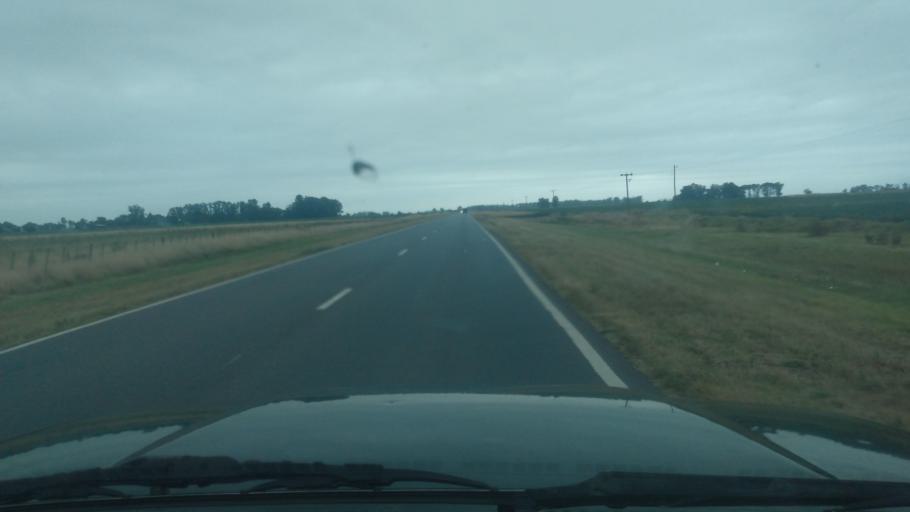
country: AR
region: Buenos Aires
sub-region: Partido de Nueve de Julio
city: Nueve de Julio
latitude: -35.4255
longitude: -60.7935
